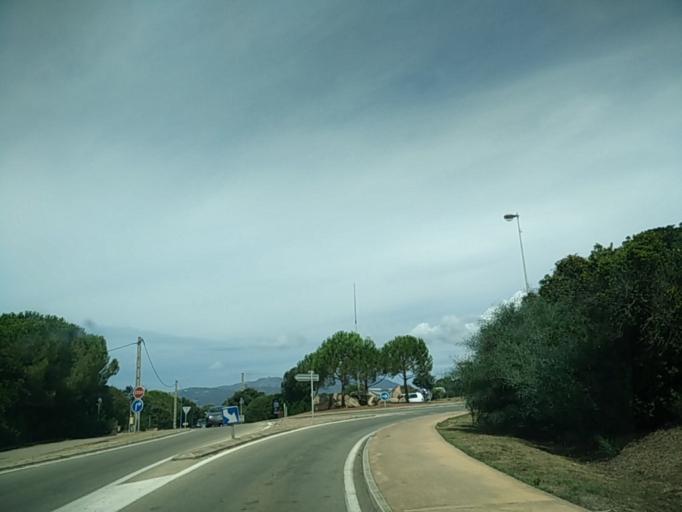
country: FR
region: Corsica
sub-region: Departement de la Corse-du-Sud
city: Pietrosella
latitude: 41.8417
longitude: 8.7683
